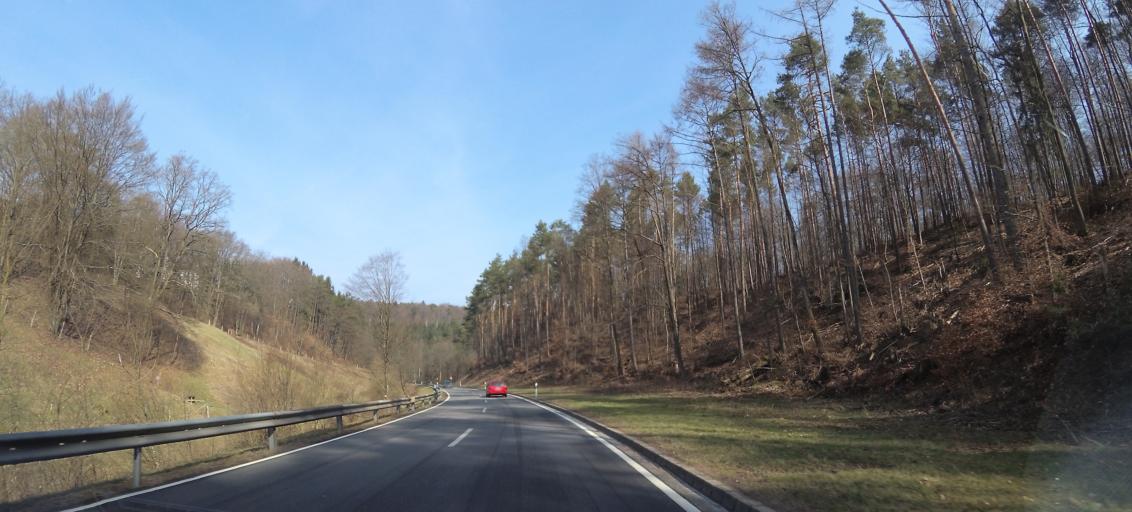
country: DE
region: Rheinland-Pfalz
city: Stelzenberg
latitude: 49.3806
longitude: 7.7433
